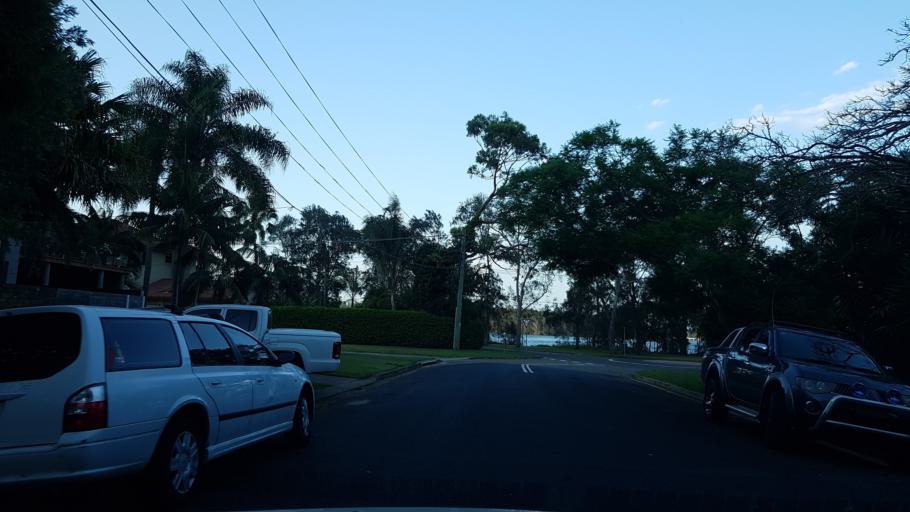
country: AU
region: New South Wales
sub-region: Warringah
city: Narrabeen
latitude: -33.7219
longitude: 151.2919
